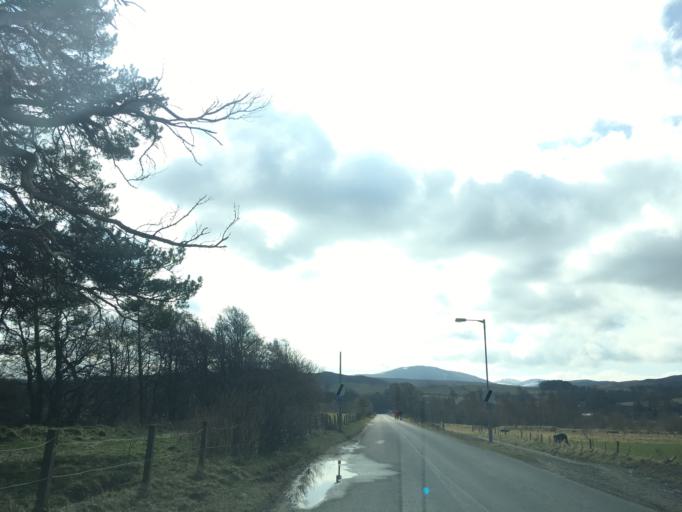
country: GB
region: Scotland
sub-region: Highland
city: Kingussie
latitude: 57.0766
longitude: -4.0510
